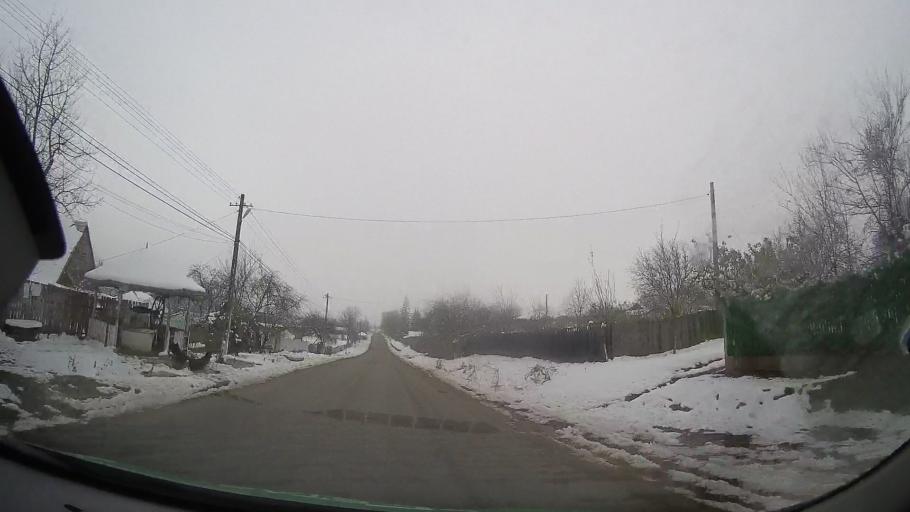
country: RO
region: Bacau
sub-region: Comuna Vultureni
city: Vultureni
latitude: 46.4016
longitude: 27.2733
